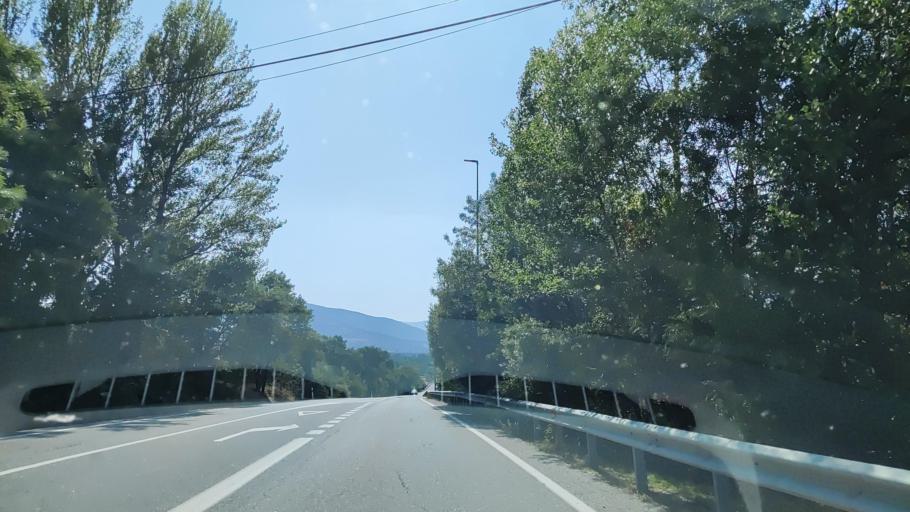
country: ES
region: Madrid
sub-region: Provincia de Madrid
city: Garganta de los Montes
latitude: 40.9420
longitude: -3.7002
